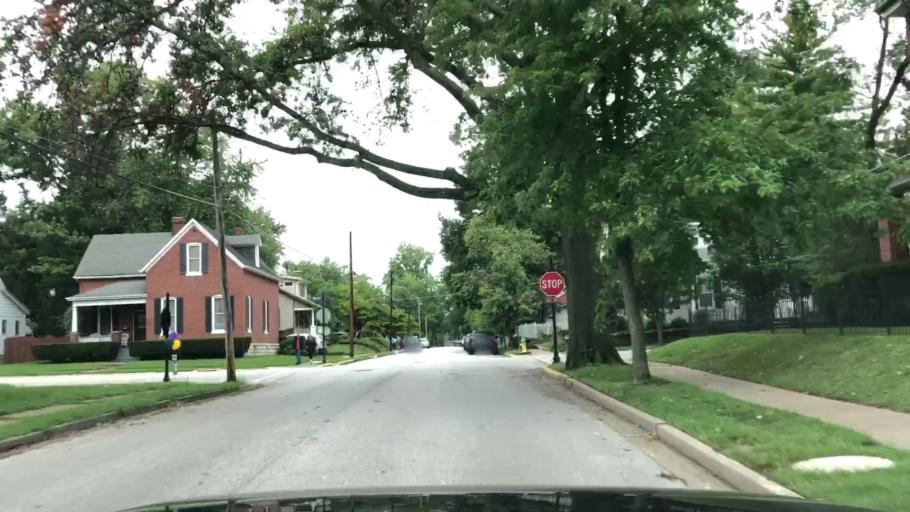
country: US
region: Missouri
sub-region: Saint Charles County
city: Saint Charles
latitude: 38.7851
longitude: -90.4872
